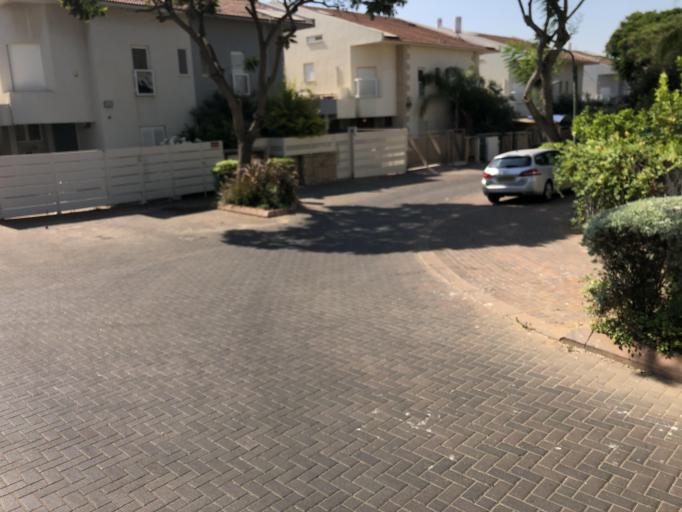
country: IL
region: Central District
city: Yehud
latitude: 32.0364
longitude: 34.8823
